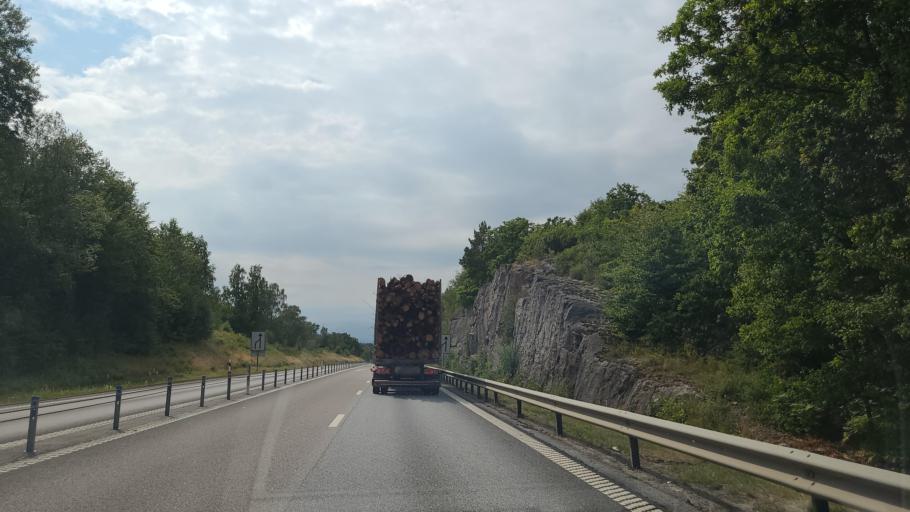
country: SE
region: Blekinge
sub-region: Ronneby Kommun
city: Brakne-Hoby
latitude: 56.2127
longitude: 15.0952
